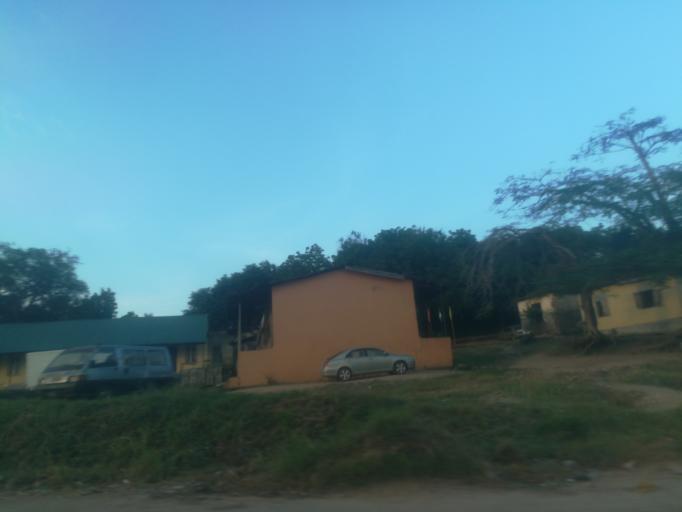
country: NG
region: Ogun
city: Abeokuta
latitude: 7.1479
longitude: 3.3373
